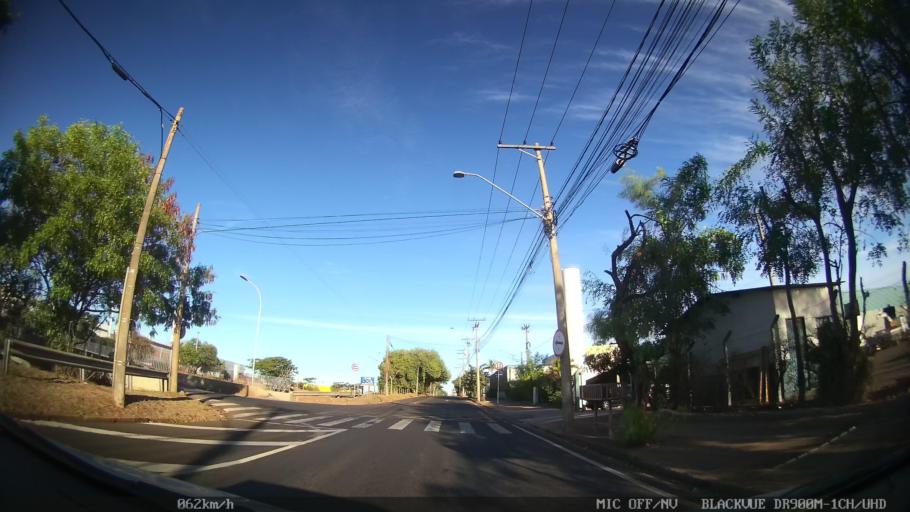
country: BR
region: Sao Paulo
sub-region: Sao Jose Do Rio Preto
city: Sao Jose do Rio Preto
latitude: -20.8498
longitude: -49.3452
